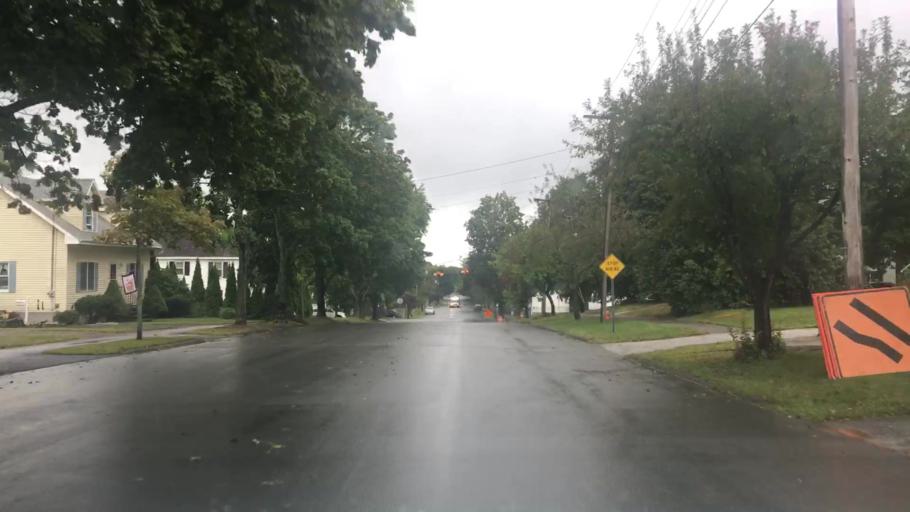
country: US
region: Maine
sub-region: Penobscot County
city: Brewer
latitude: 44.8151
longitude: -68.7599
